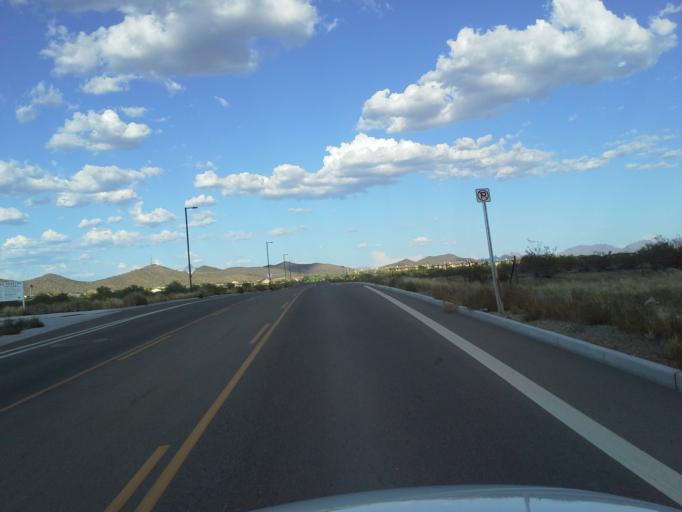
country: US
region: Arizona
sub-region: Maricopa County
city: Anthem
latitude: 33.7838
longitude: -112.1244
